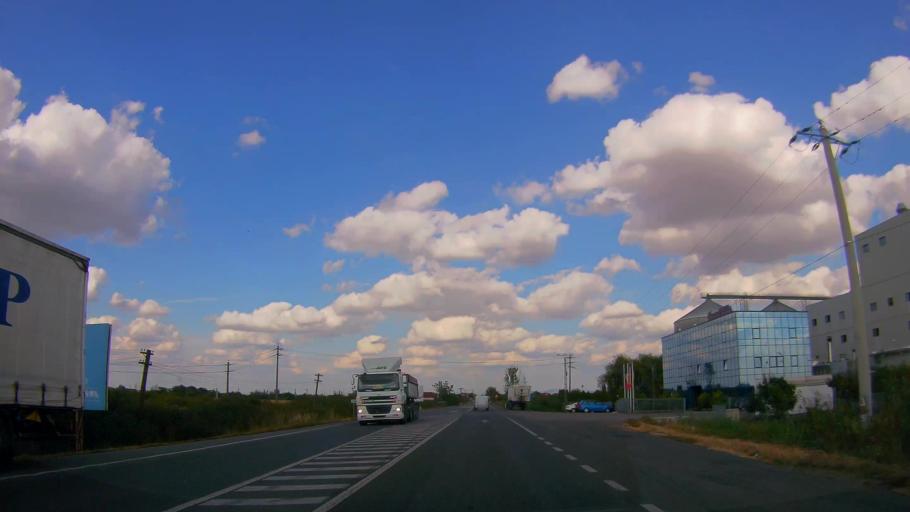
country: RO
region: Satu Mare
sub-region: Comuna Botiz
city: Botiz
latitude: 47.8205
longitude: 22.9377
